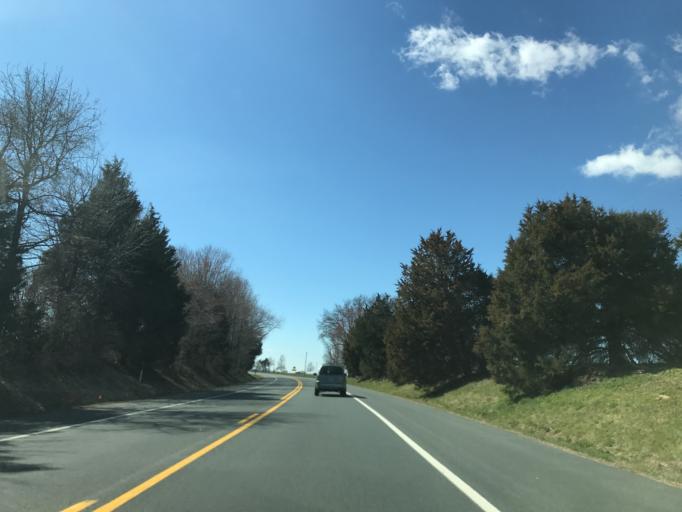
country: US
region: Maryland
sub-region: Queen Anne's County
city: Kingstown
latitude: 39.2568
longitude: -75.9954
